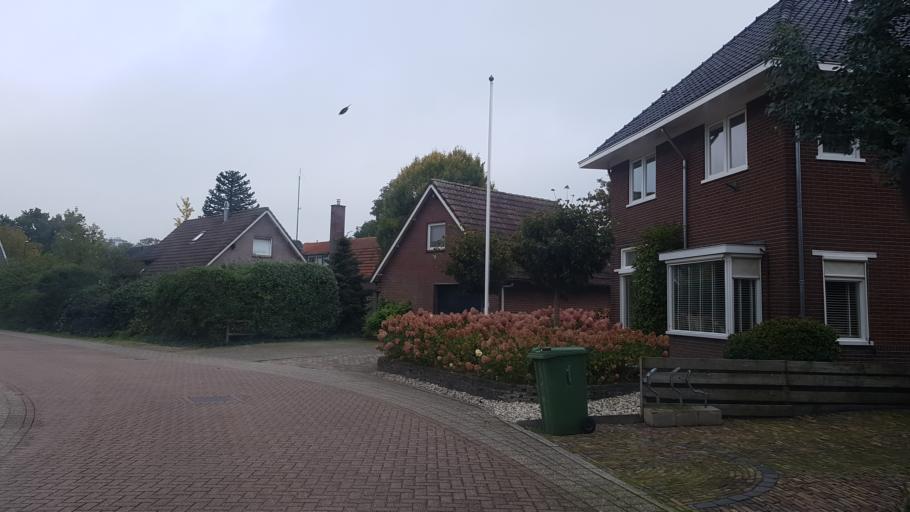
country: NL
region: Gelderland
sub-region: Gemeente Apeldoorn
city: Apeldoorn
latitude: 52.2148
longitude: 5.9931
